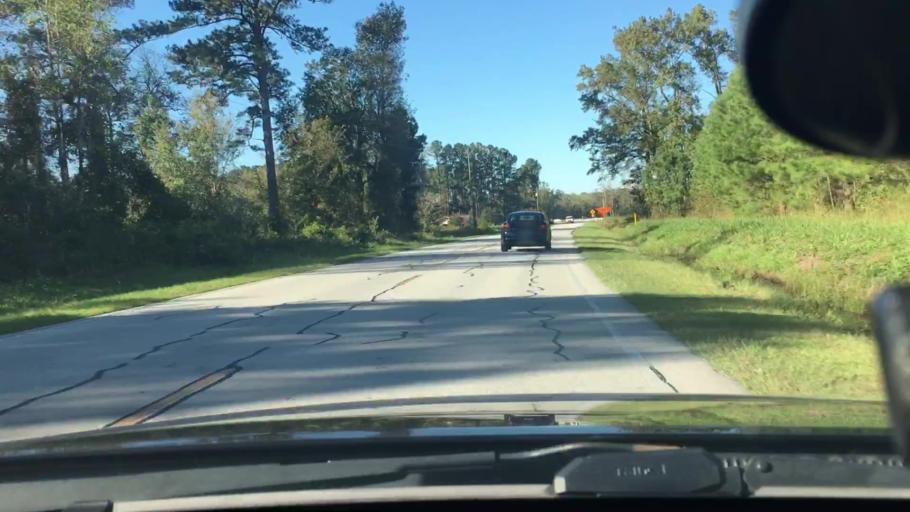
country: US
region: North Carolina
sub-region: Craven County
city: Vanceboro
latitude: 35.2842
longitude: -77.1543
